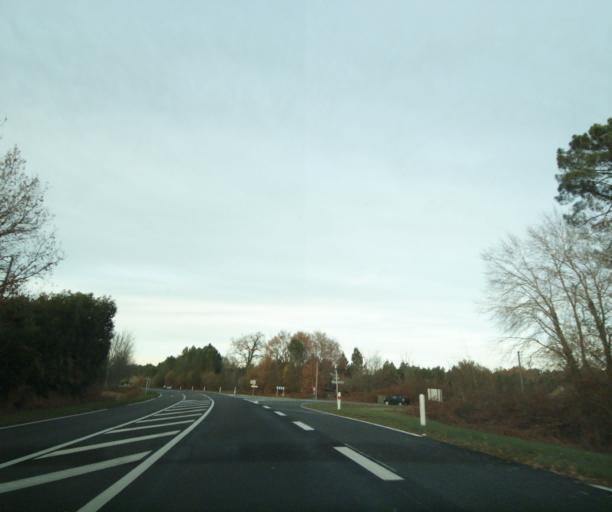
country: FR
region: Aquitaine
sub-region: Departement de la Gironde
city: Bazas
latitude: 44.3359
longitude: -0.2348
